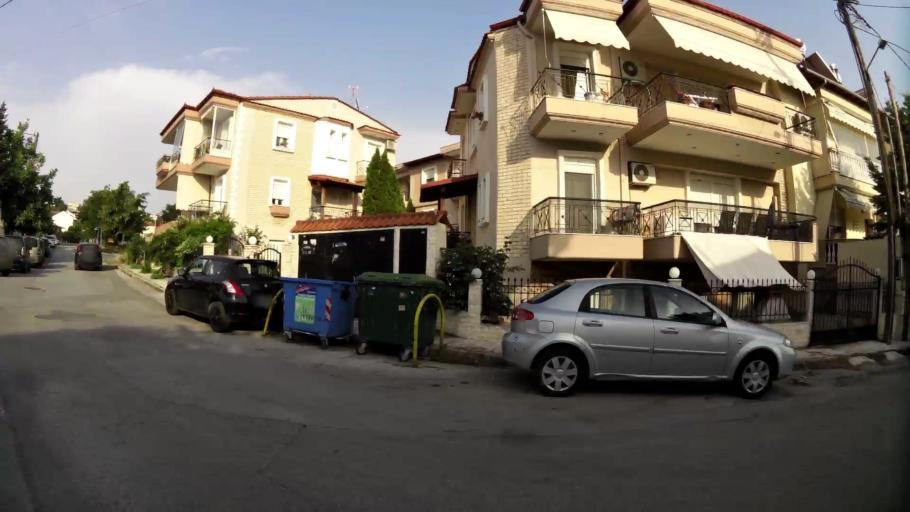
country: GR
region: Central Macedonia
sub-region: Nomos Thessalonikis
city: Oraiokastro
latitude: 40.7214
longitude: 22.9082
